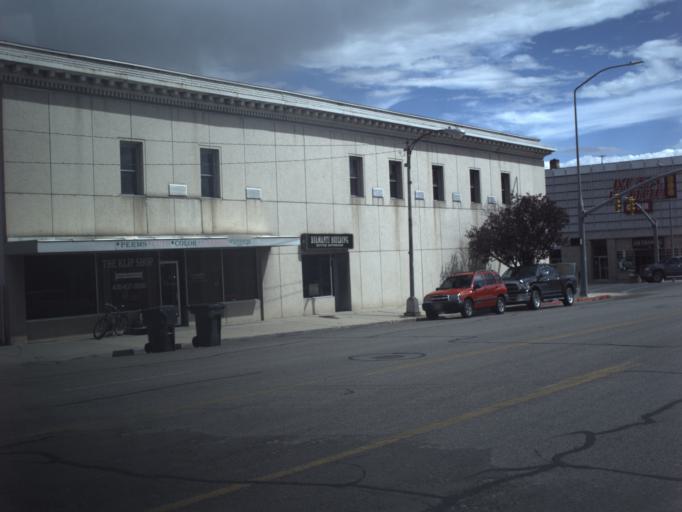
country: US
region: Utah
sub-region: Carbon County
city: Price
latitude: 39.6001
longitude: -110.8113
